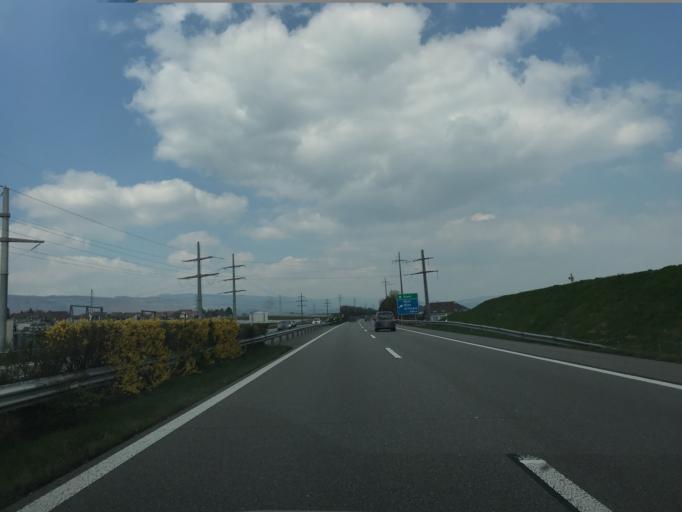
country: CH
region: Vaud
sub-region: Nyon District
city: Trelex
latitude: 46.3844
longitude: 6.2034
